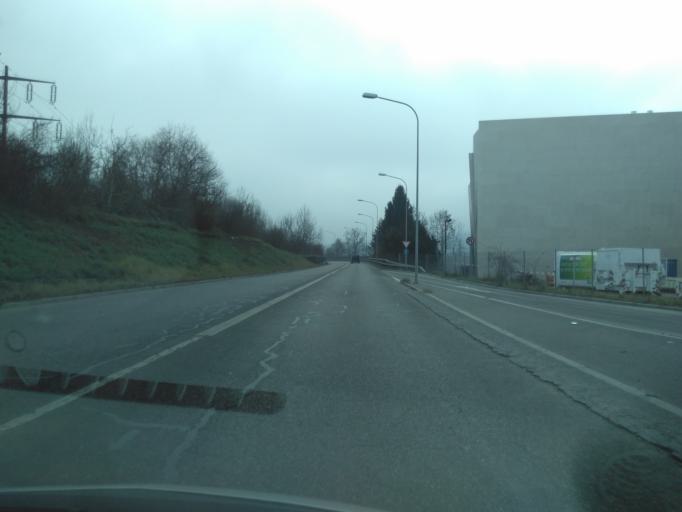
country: CH
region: Zurich
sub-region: Bezirk Zuerich
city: Zuerich (Kreis 12) / Auzelg
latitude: 47.4151
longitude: 8.5662
